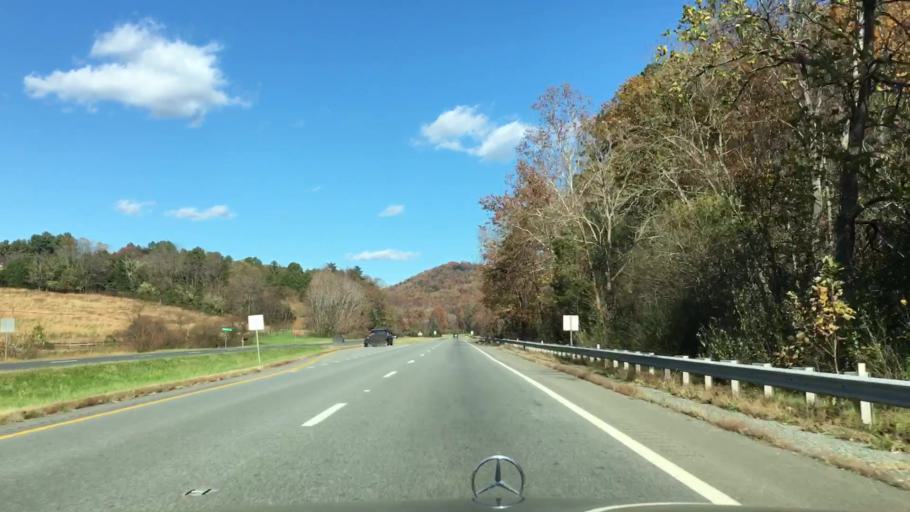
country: US
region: Virginia
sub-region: Albemarle County
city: Crozet
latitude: 37.9707
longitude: -78.6134
